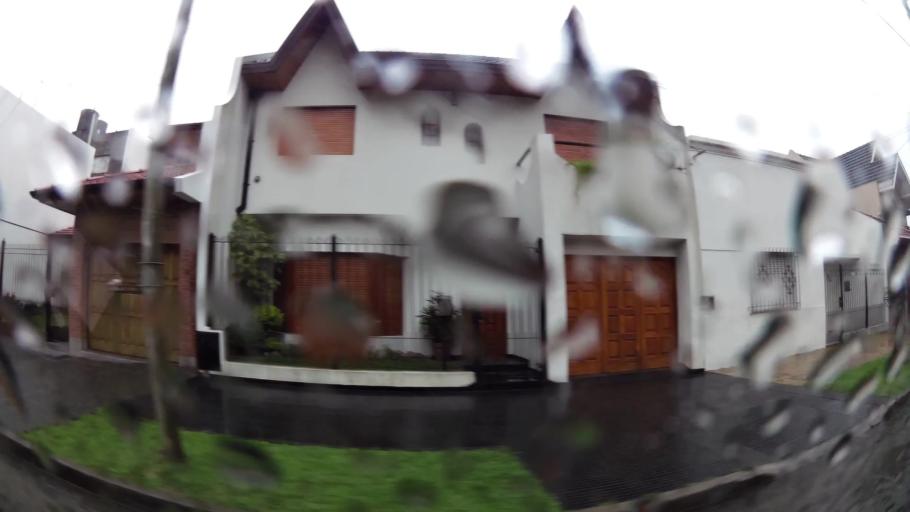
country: AR
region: Buenos Aires
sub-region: Partido de Lanus
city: Lanus
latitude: -34.7128
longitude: -58.3994
